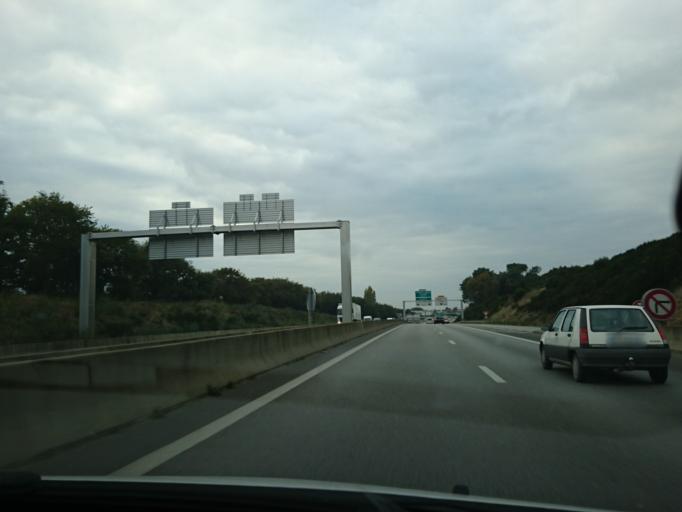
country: FR
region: Brittany
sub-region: Departement du Morbihan
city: Theix
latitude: 47.6424
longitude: -2.6895
